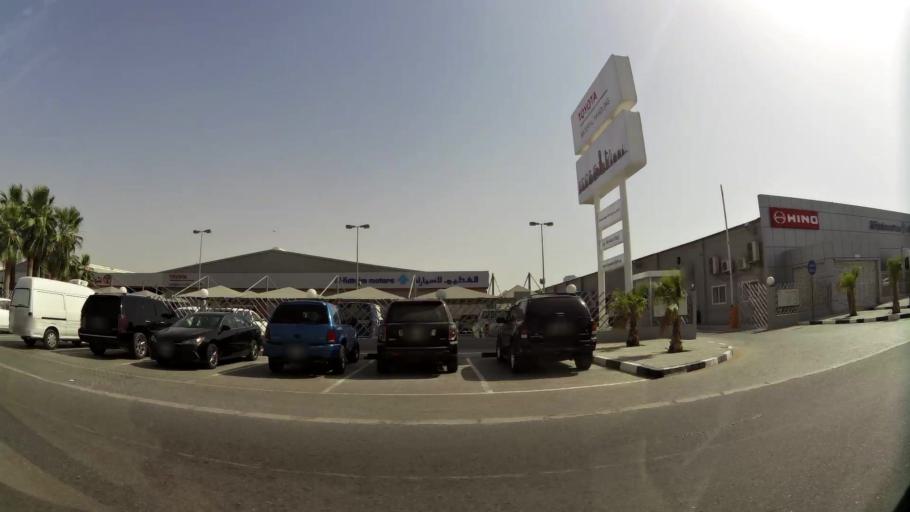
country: AE
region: Ash Shariqah
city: Sharjah
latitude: 25.2350
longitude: 55.3625
